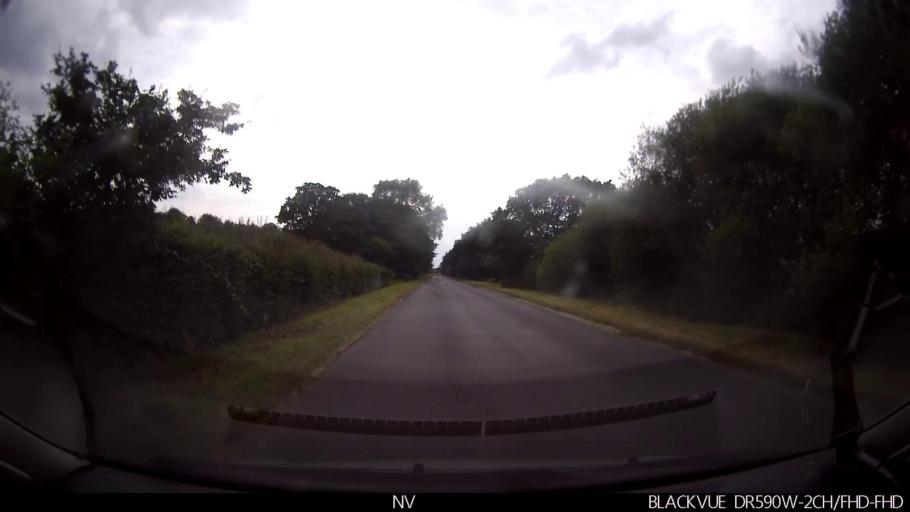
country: GB
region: England
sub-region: North Yorkshire
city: Strensall
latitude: 54.0470
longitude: -0.9848
